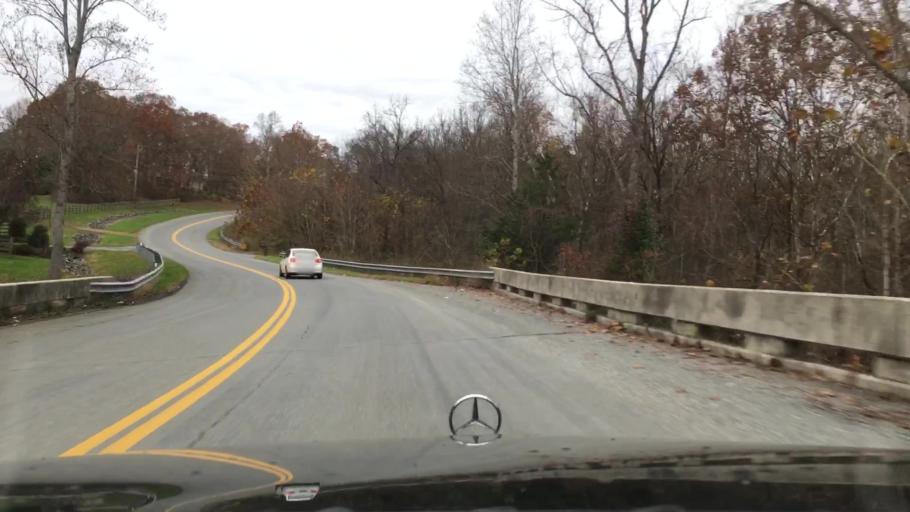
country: US
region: Virginia
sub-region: Campbell County
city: Timberlake
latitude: 37.2900
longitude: -79.2744
